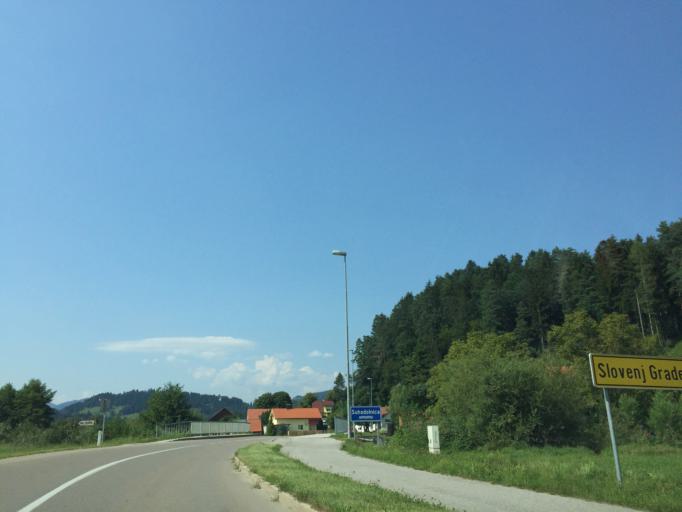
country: SI
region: Slovenj Gradec
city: Slovenj Gradec
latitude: 46.4880
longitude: 15.0755
